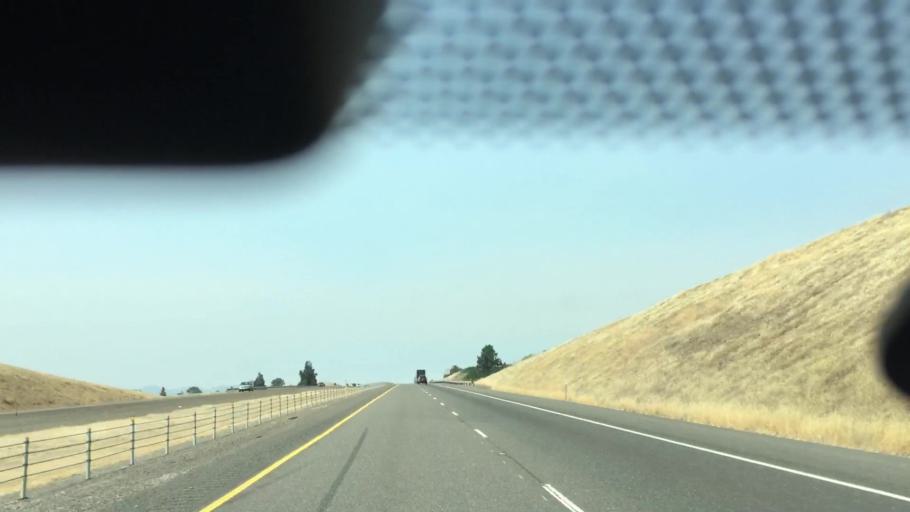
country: US
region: Oregon
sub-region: Jackson County
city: Ashland
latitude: 42.2023
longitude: -122.6831
